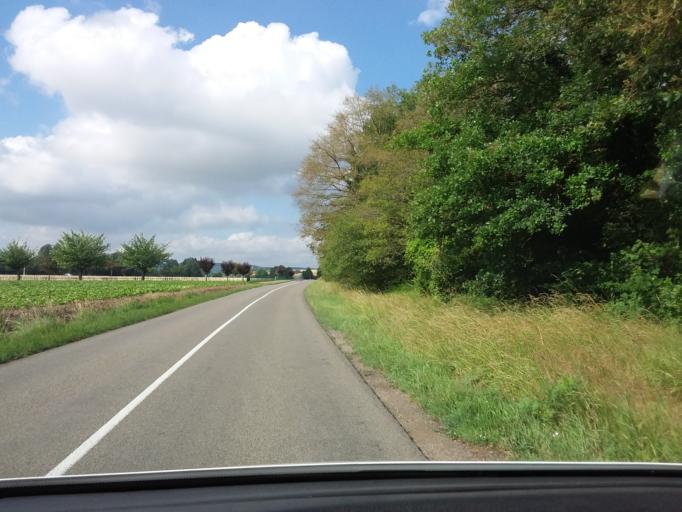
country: FR
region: Champagne-Ardenne
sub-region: Departement de la Marne
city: Cormicy
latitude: 49.4060
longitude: 3.8112
